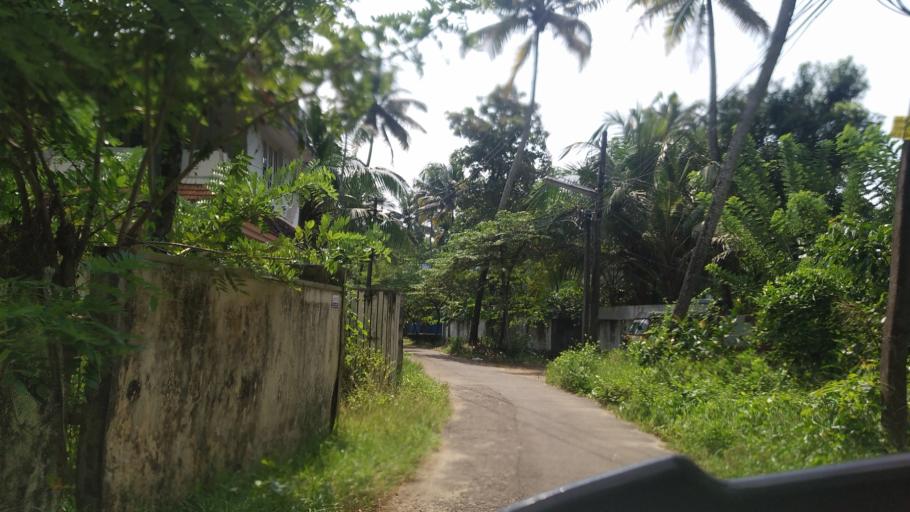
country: IN
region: Kerala
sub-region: Ernakulam
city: Elur
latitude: 10.0589
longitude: 76.2162
